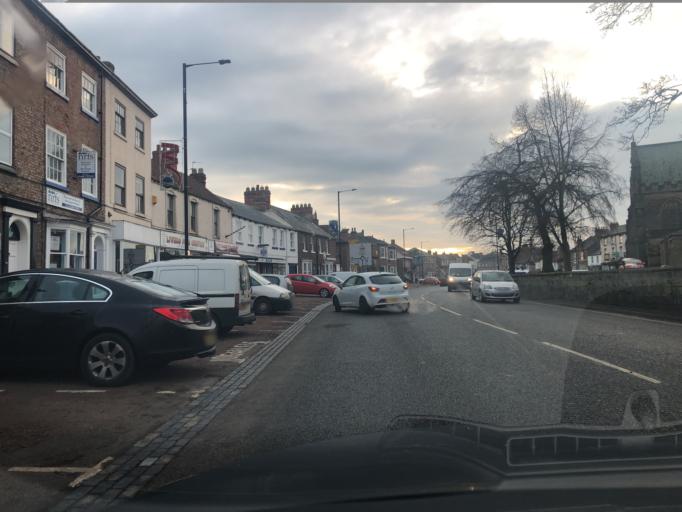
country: GB
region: England
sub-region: North Yorkshire
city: Northallerton
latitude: 54.3428
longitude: -1.4366
